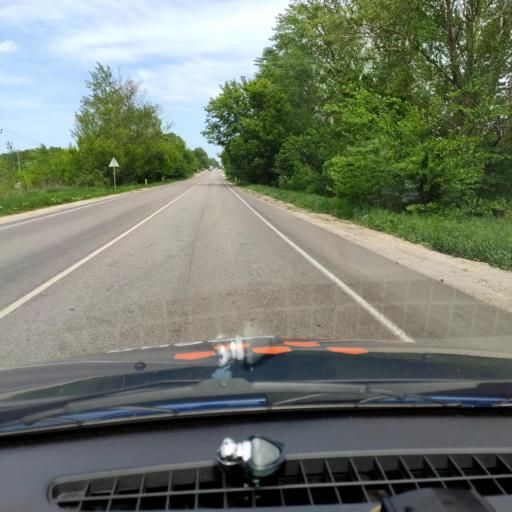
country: RU
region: Voronezj
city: Maslovka
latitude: 51.5309
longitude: 39.3115
